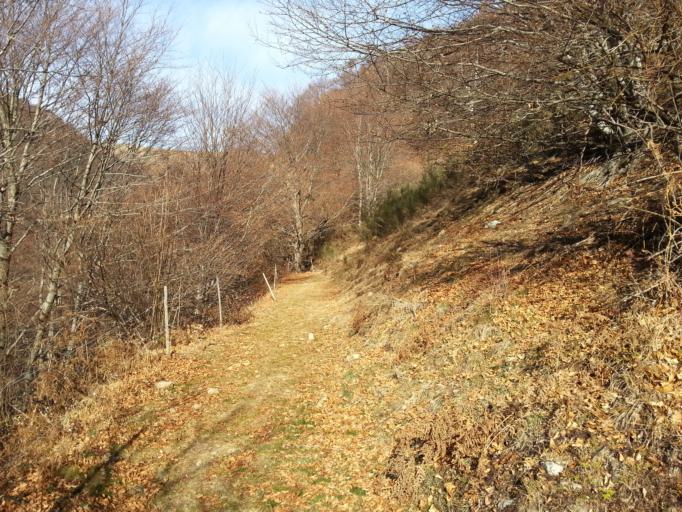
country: CH
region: Ticino
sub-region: Lugano District
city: Gravesano
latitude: 46.0663
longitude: 8.8777
